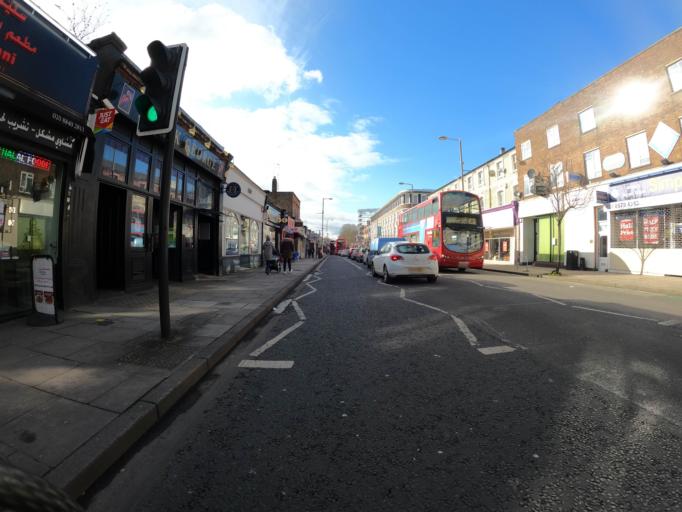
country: GB
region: England
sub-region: Greater London
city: Ealing
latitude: 51.5112
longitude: -0.3172
